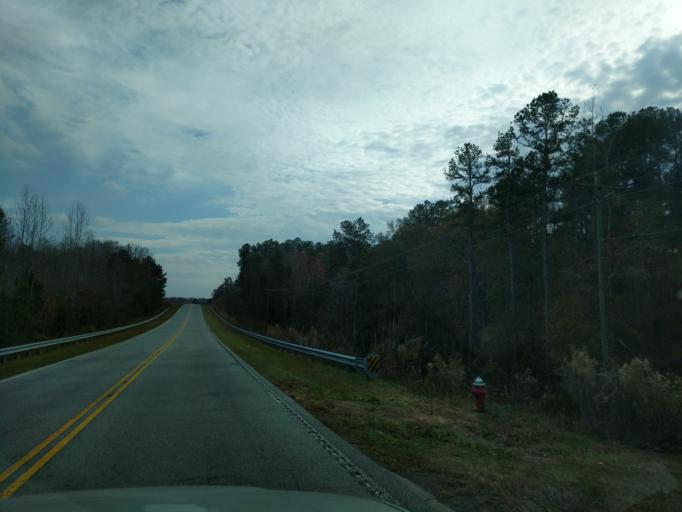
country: US
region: Georgia
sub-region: Franklin County
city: Gumlog
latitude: 34.5071
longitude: -83.0420
